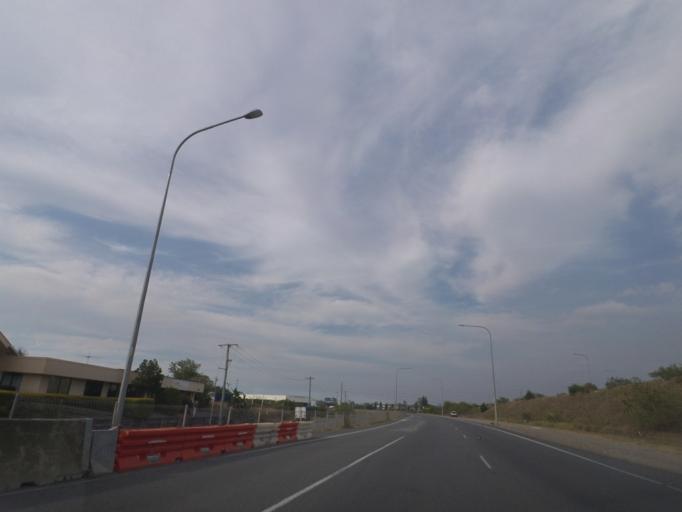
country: AU
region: Queensland
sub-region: Brisbane
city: Rocklea
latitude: -27.5558
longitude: 153.0081
